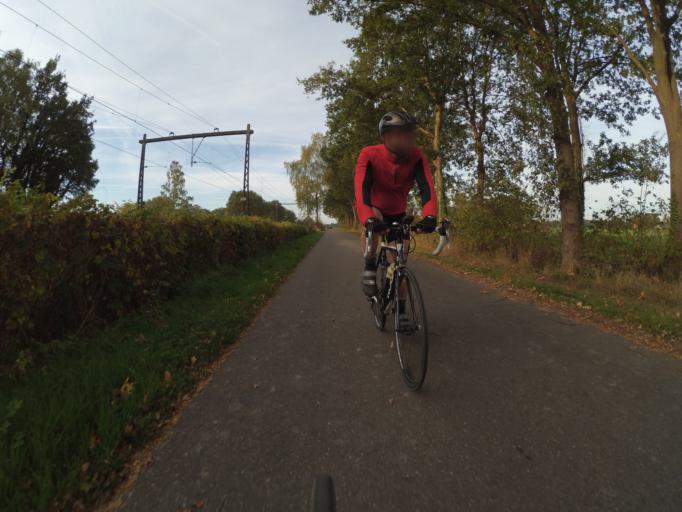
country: NL
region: Gelderland
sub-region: Gemeente Lochem
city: Harfsen
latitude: 52.2572
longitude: 6.3183
